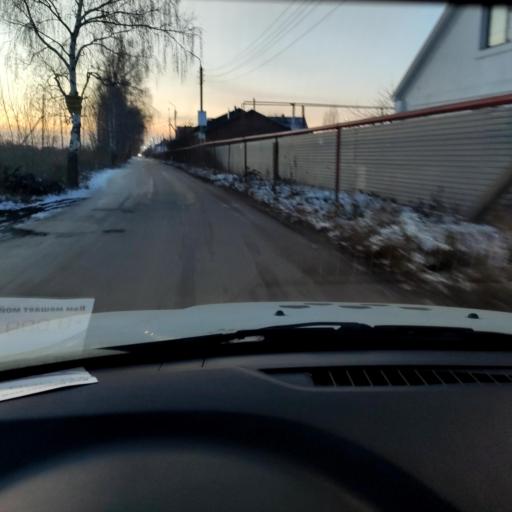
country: RU
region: Samara
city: Tol'yatti
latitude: 53.5601
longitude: 49.3868
